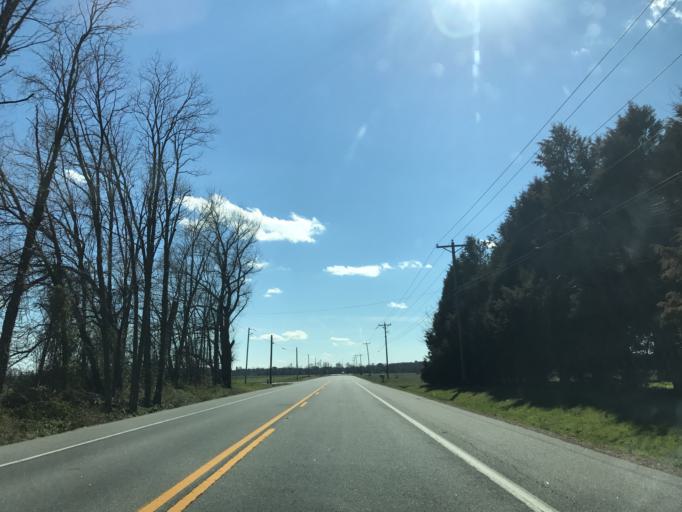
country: US
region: Maryland
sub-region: Kent County
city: Rock Hall
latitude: 39.1692
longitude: -76.1994
